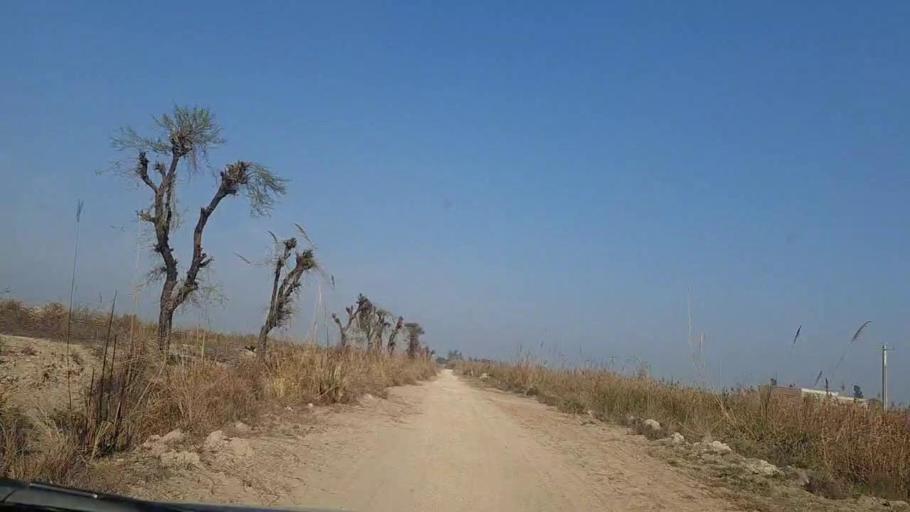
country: PK
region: Sindh
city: Sakrand
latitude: 26.0852
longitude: 68.3641
